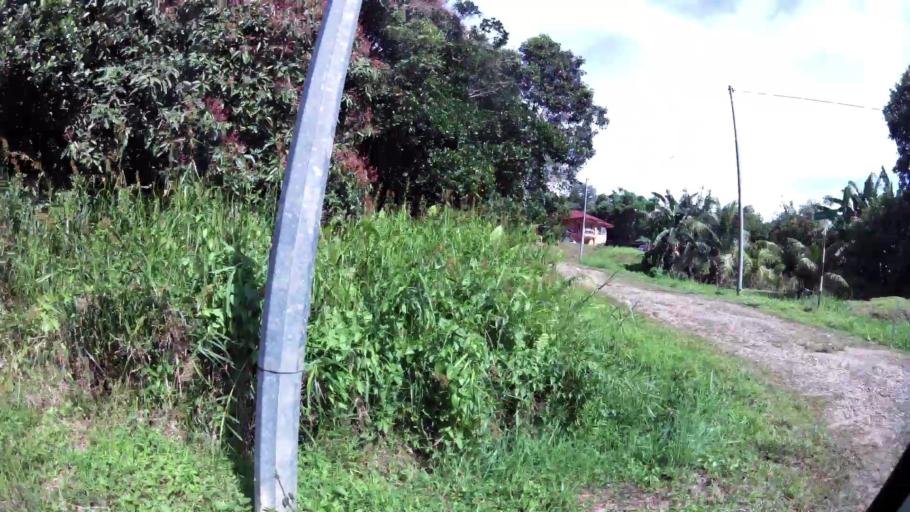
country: BN
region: Brunei and Muara
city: Bandar Seri Begawan
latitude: 5.0211
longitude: 115.0494
